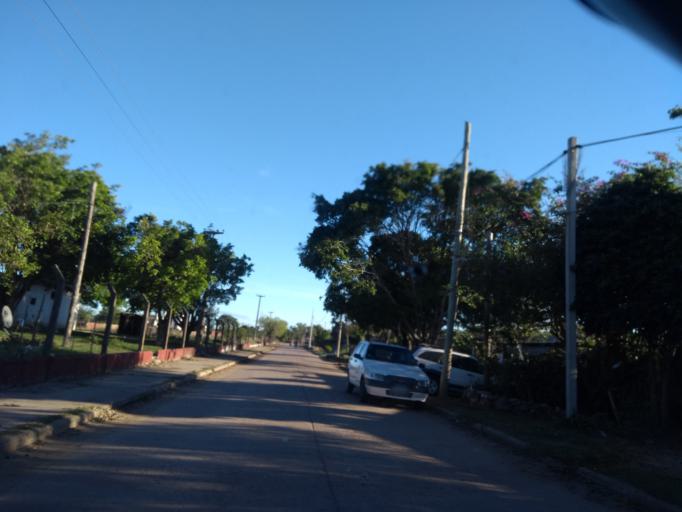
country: AR
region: Chaco
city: Barranqueras
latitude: -27.4990
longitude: -58.9326
